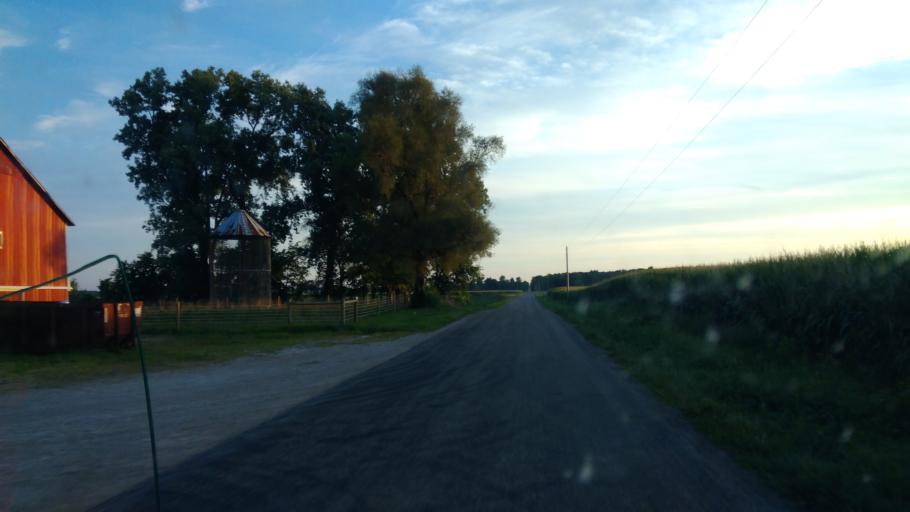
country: US
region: Indiana
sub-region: Adams County
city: Berne
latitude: 40.6658
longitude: -85.0324
